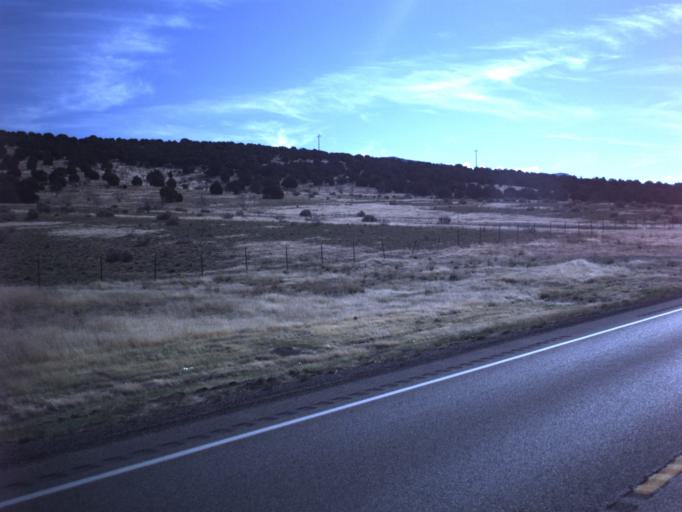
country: US
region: Utah
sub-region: Sanpete County
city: Gunnison
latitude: 39.3296
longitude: -111.9138
